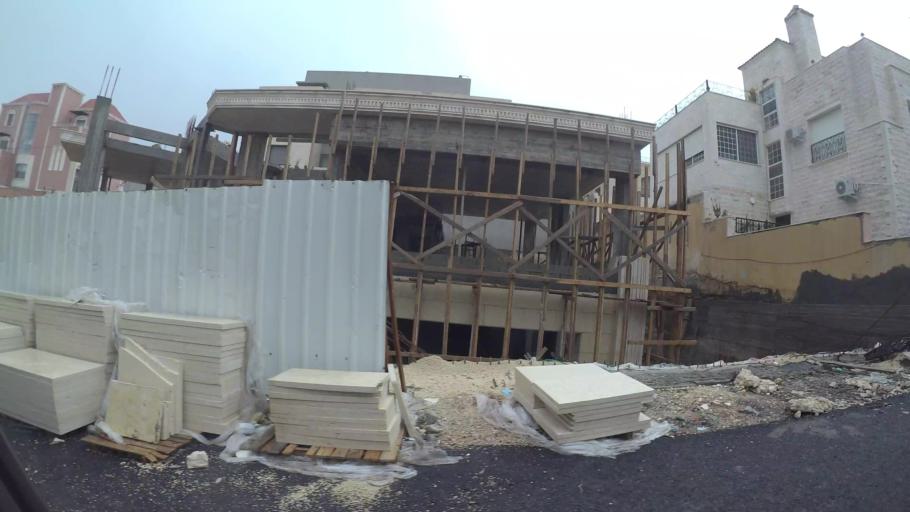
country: JO
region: Amman
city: Al Jubayhah
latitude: 32.0076
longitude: 35.8224
